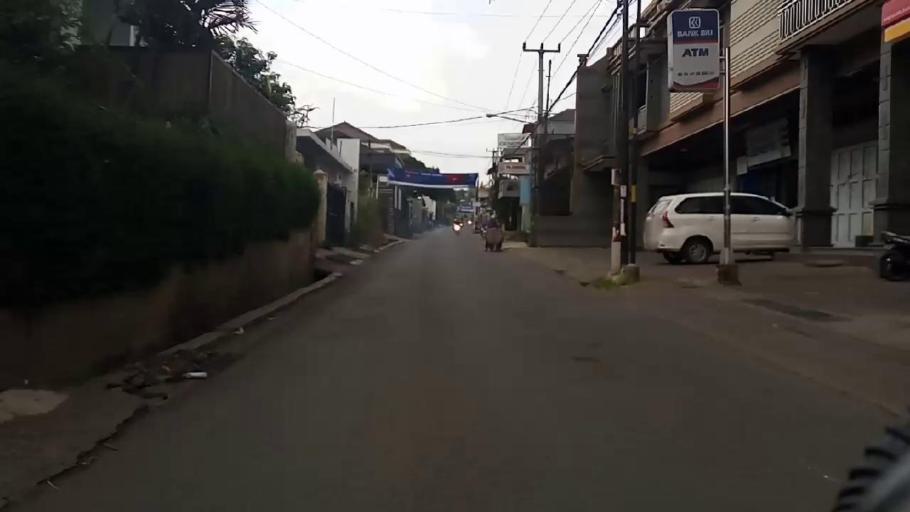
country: ID
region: West Java
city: Cimahi
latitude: -6.8618
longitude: 107.5764
